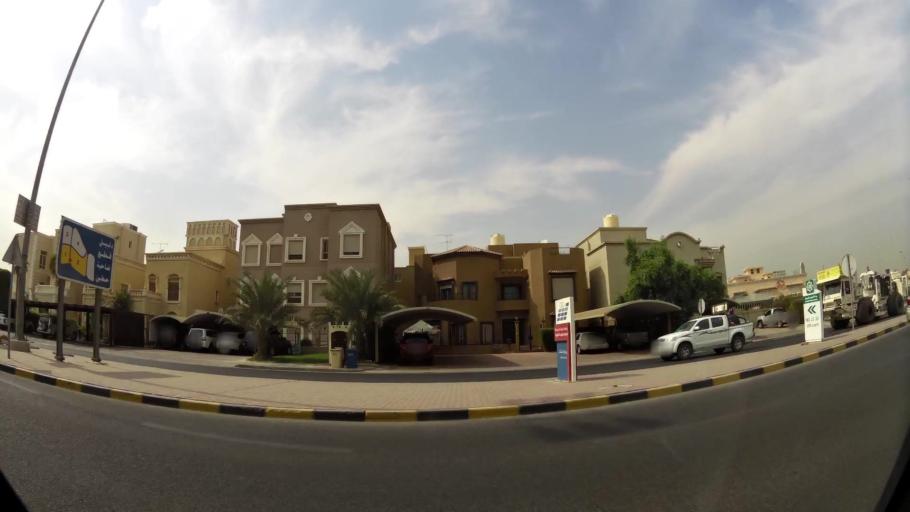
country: KW
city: Bayan
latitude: 29.2870
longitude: 48.0195
